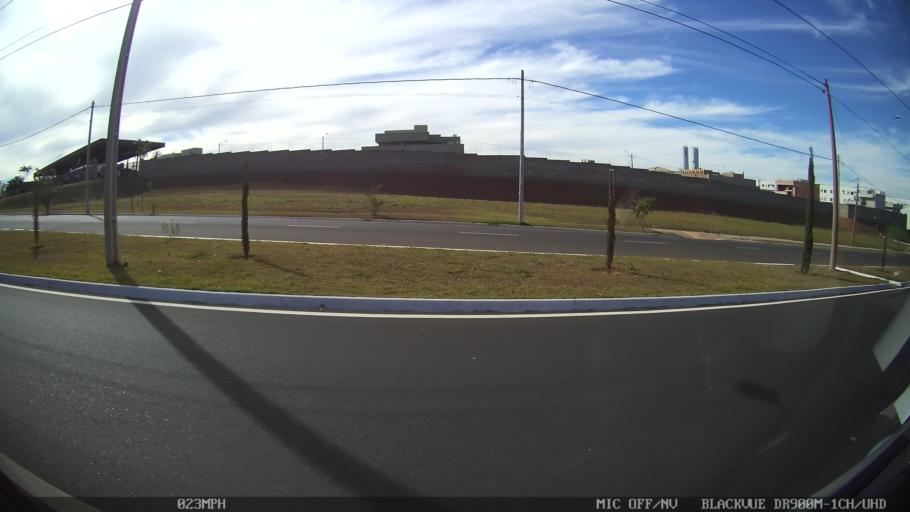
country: BR
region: Sao Paulo
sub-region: Catanduva
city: Catanduva
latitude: -21.1188
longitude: -48.9785
